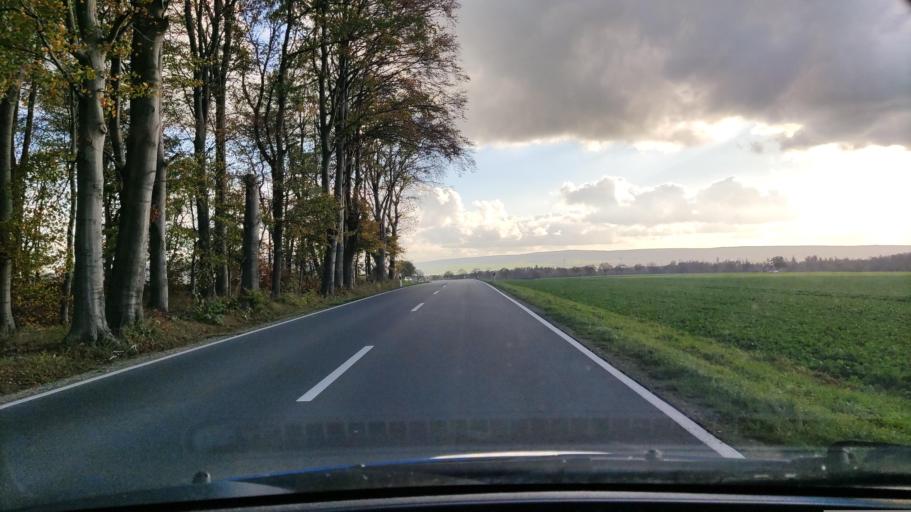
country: DE
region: Lower Saxony
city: Stadtoldendorf
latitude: 51.9046
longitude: 9.6126
